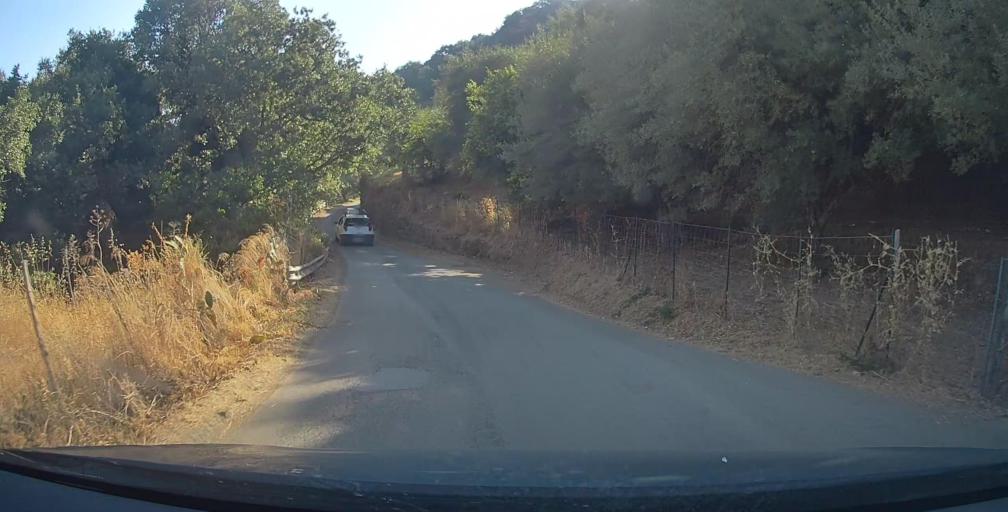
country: IT
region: Sicily
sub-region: Messina
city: San Piero Patti
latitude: 38.0591
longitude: 14.9968
